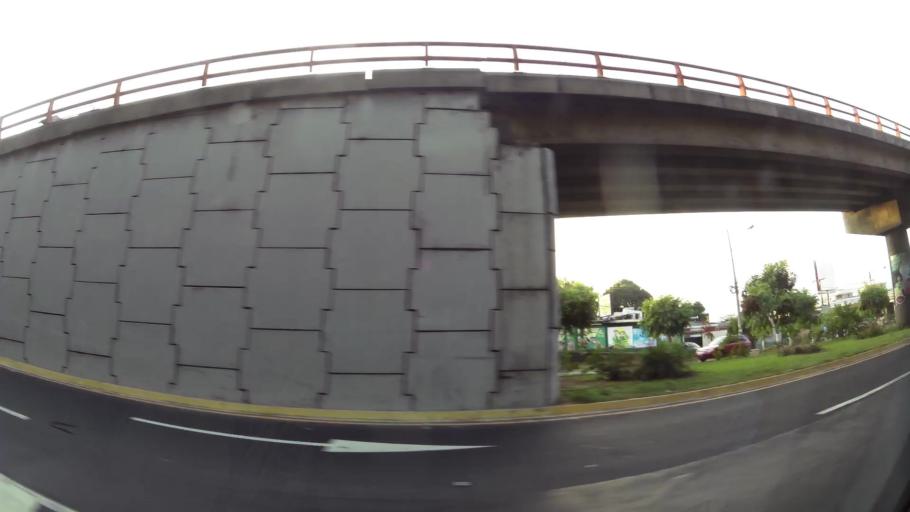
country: SV
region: San Salvador
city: San Salvador
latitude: 13.6837
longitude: -89.2178
